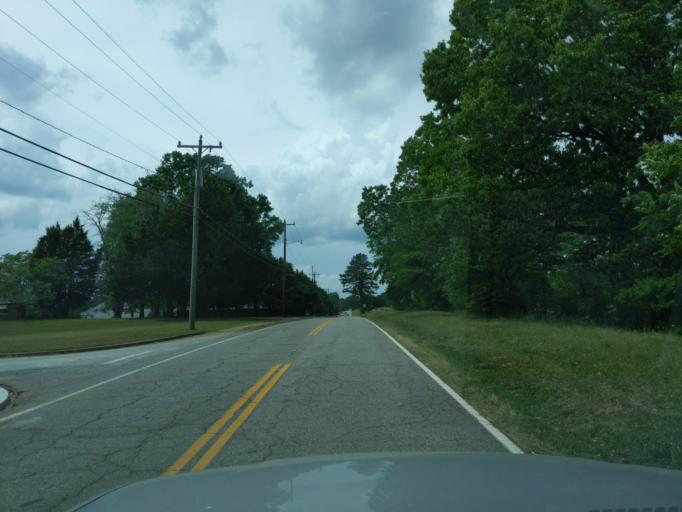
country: US
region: South Carolina
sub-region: Spartanburg County
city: Wellford
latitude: 34.9517
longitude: -82.0929
